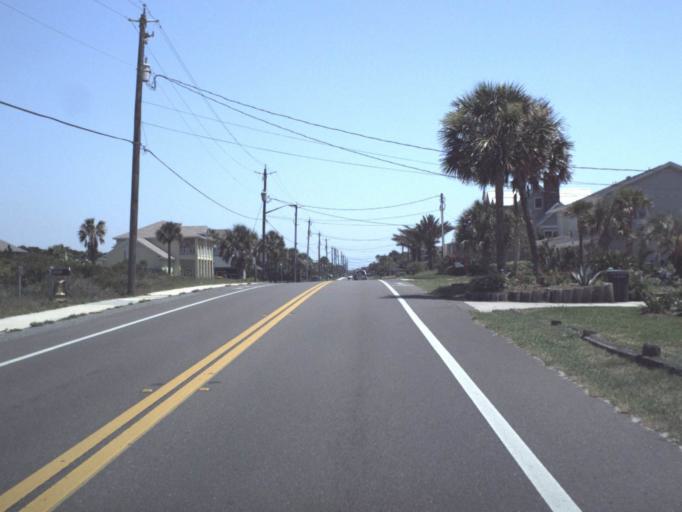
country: US
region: Florida
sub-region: Nassau County
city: Fernandina Beach
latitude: 30.6442
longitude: -81.4356
